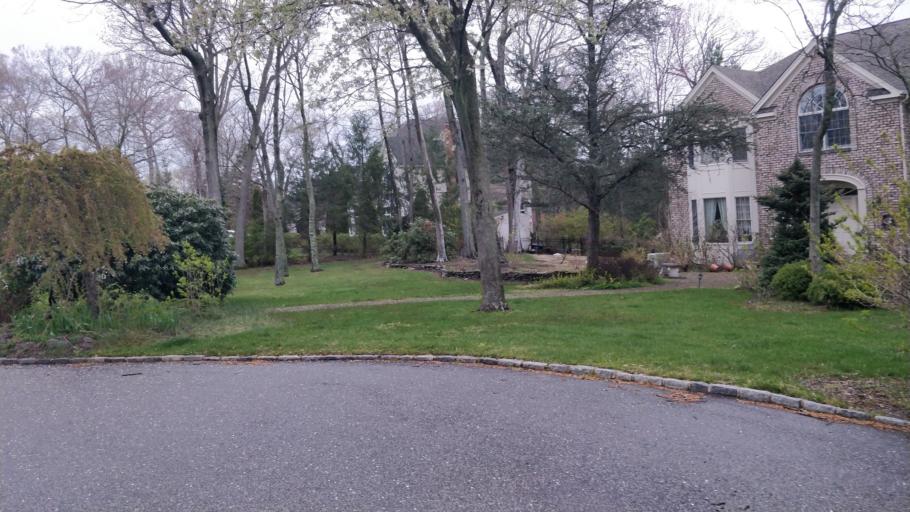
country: US
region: New York
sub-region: Suffolk County
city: Port Jefferson
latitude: 40.9536
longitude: -73.0876
